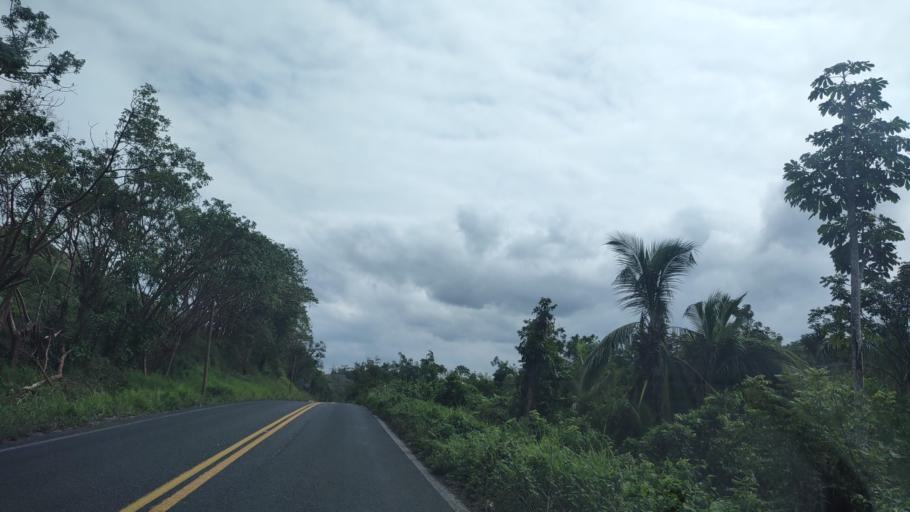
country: MX
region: Veracruz
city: Papantla de Olarte
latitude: 20.4638
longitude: -97.2720
